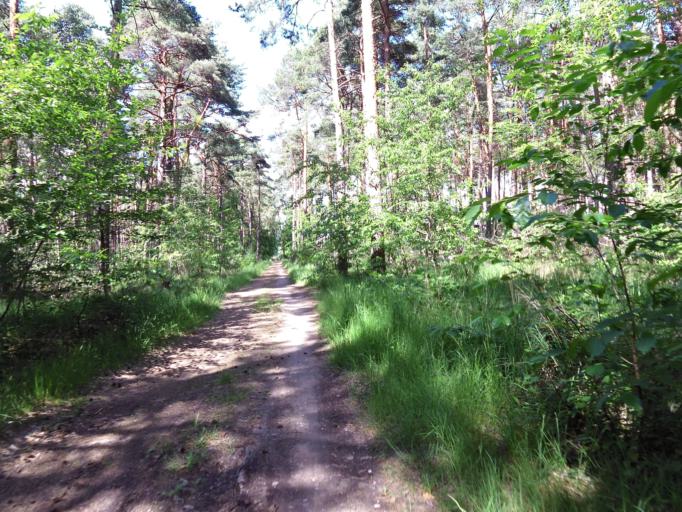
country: DE
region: Rheinland-Pfalz
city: Hassloch
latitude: 49.3426
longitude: 8.2323
